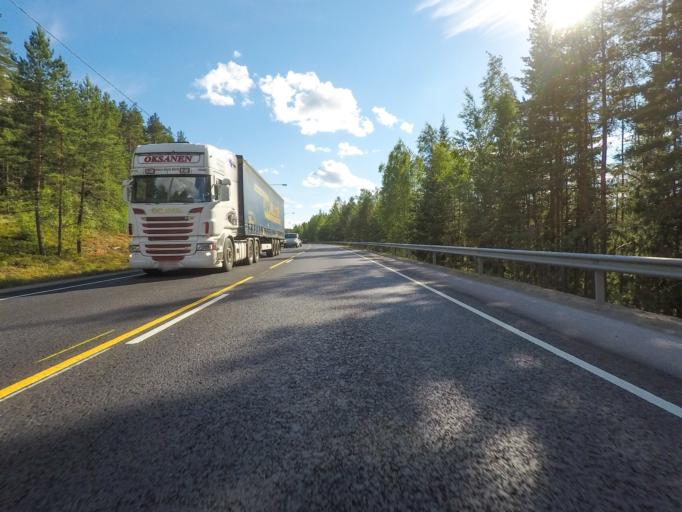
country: FI
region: Uusimaa
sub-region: Helsinki
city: Vihti
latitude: 60.3464
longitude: 24.3133
